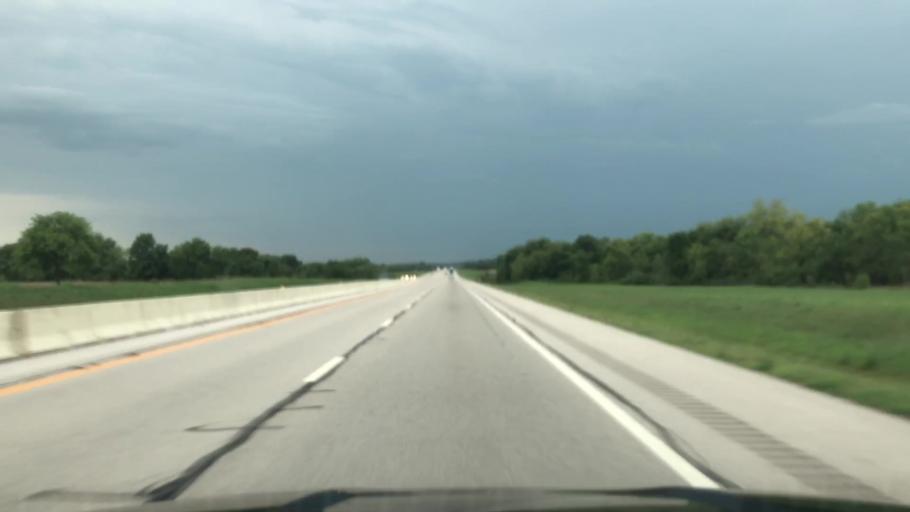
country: US
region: Oklahoma
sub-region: Rogers County
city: Bushyhead
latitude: 36.3759
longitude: -95.4390
